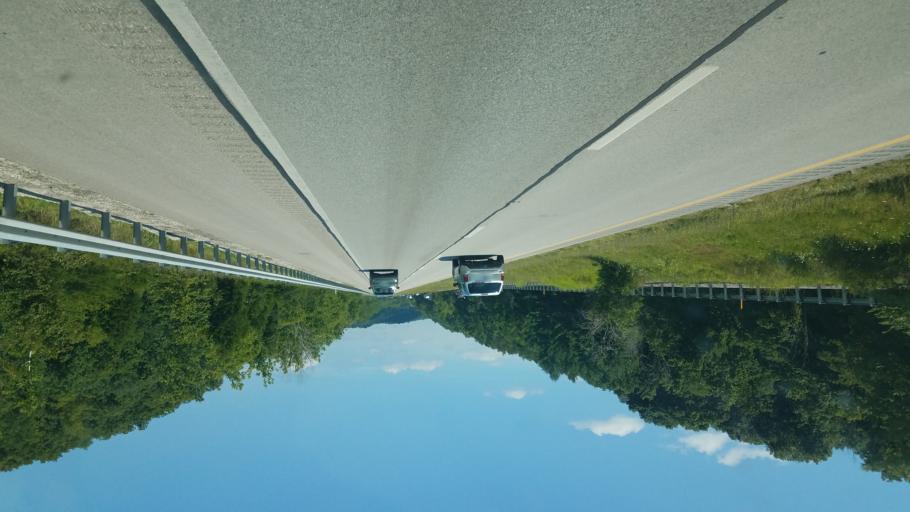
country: US
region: West Virginia
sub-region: Jackson County
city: Ripley
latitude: 38.6929
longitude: -81.6405
